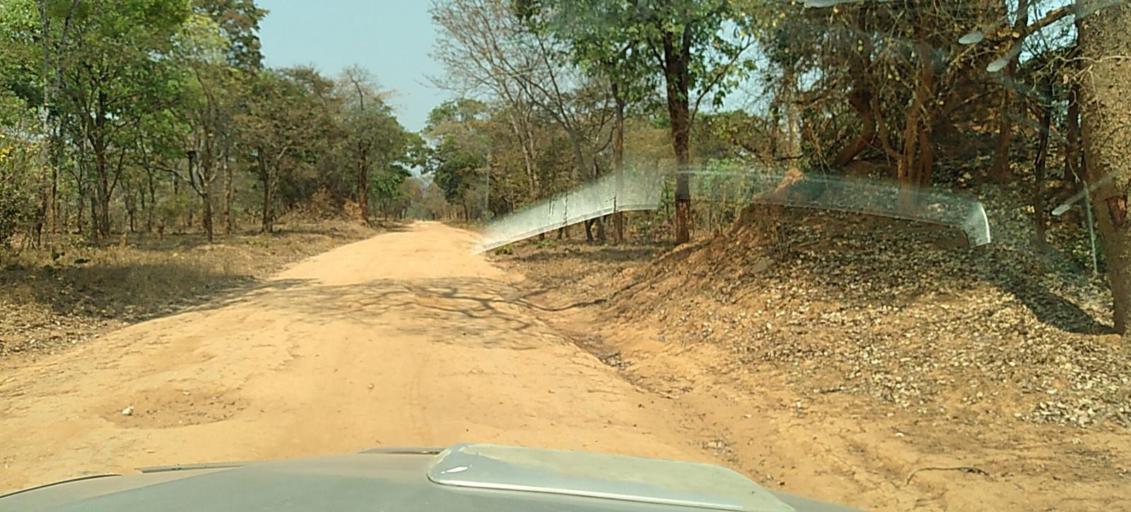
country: ZM
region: North-Western
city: Kasempa
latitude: -13.6657
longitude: 26.2842
